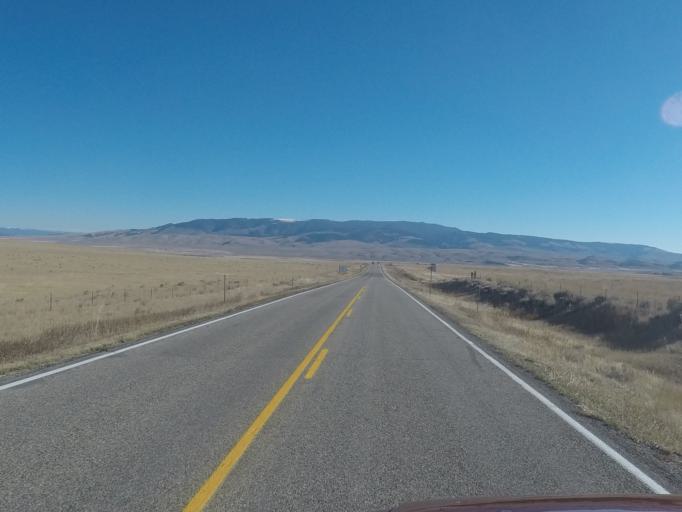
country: US
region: Montana
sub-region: Meagher County
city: White Sulphur Springs
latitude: 46.3977
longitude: -110.9651
